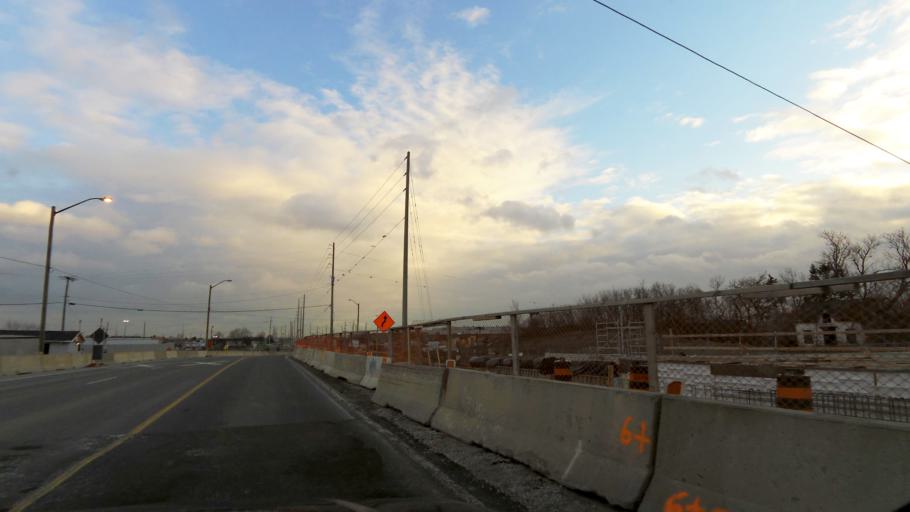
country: CA
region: Ontario
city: Brampton
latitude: 43.7084
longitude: -79.6712
